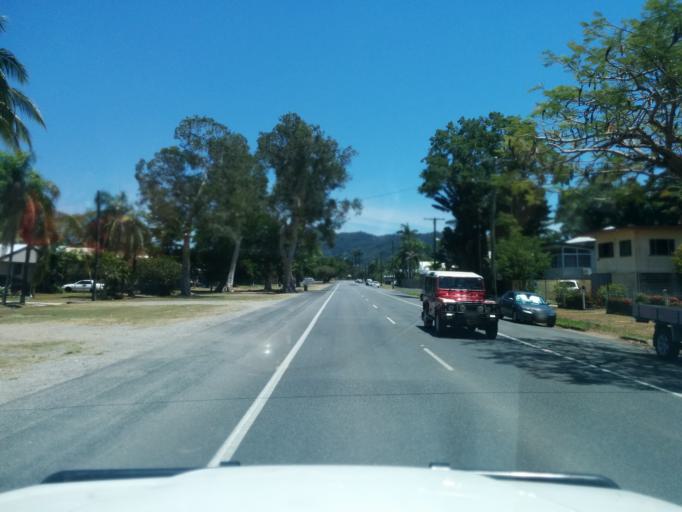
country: AU
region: Queensland
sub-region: Cairns
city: Cairns
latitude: -16.9159
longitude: 145.7569
